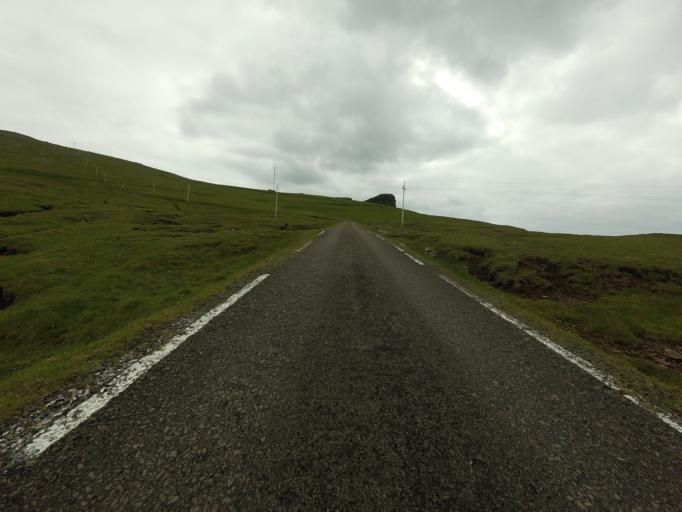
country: FO
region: Suduroy
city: Vagur
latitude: 61.4287
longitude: -6.7564
